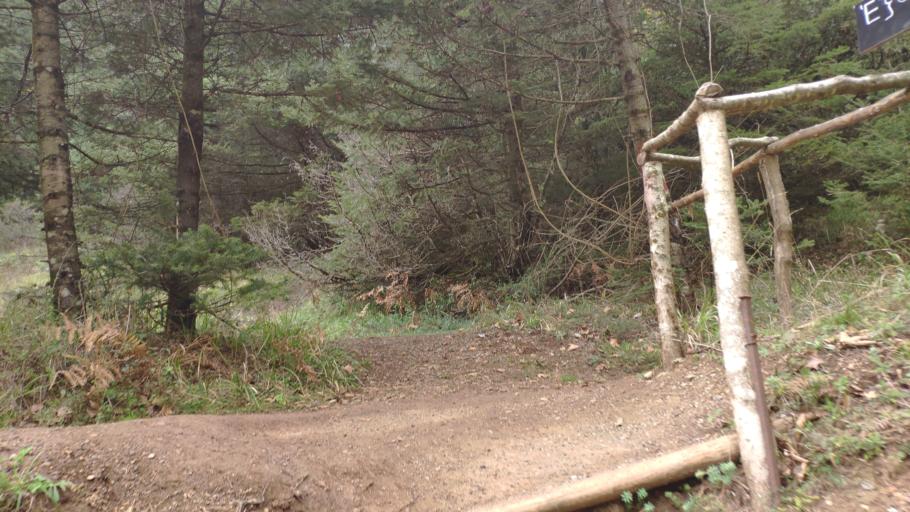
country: GR
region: Central Greece
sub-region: Nomos Fthiotidos
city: Stavros
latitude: 38.7342
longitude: 22.3336
